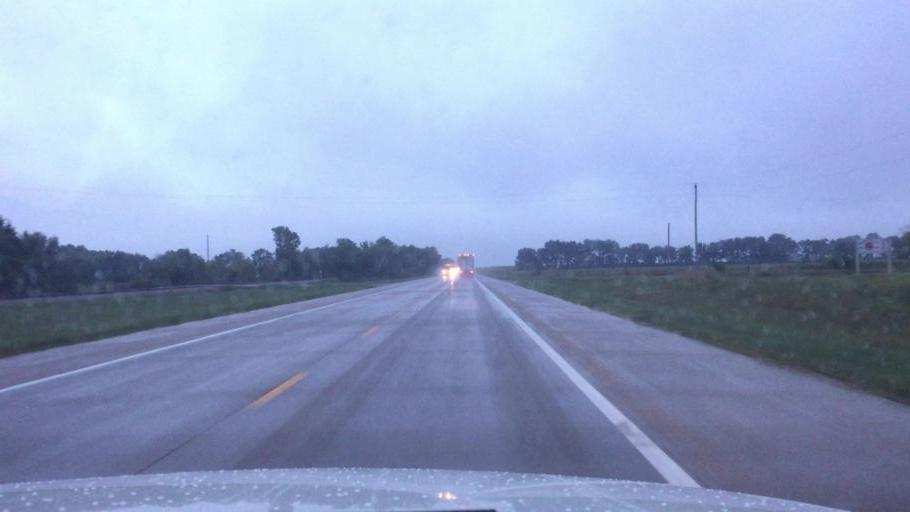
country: US
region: Kansas
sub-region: Neosho County
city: Chanute
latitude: 37.5444
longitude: -95.4708
